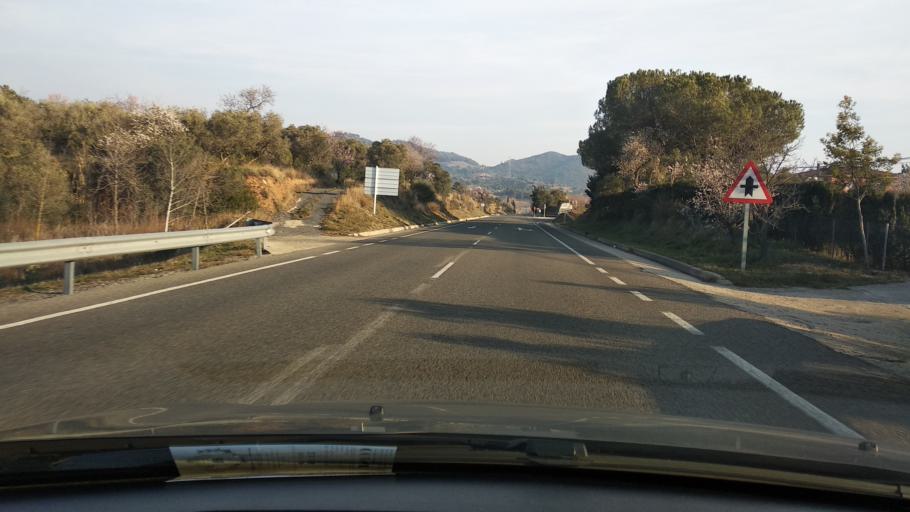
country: ES
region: Catalonia
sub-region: Provincia de Tarragona
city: Alforja
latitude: 41.2093
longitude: 0.9836
